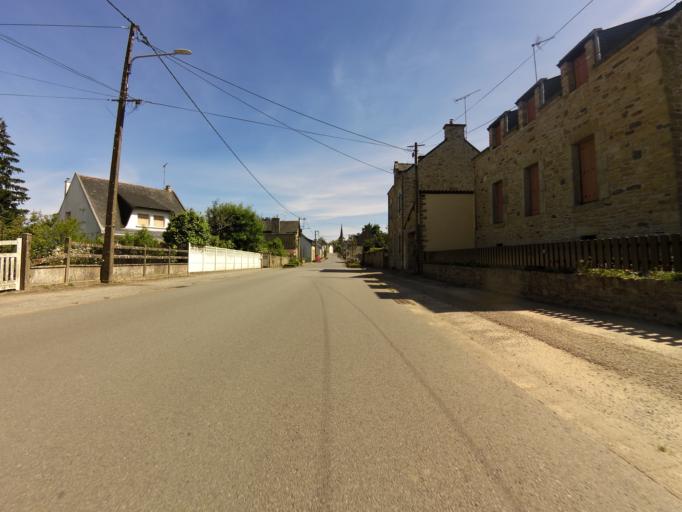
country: FR
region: Brittany
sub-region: Departement du Morbihan
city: Malansac
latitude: 47.6804
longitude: -2.2999
